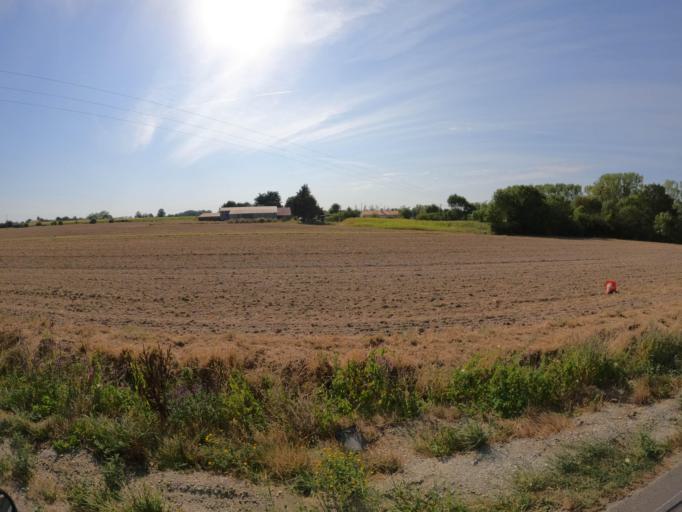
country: FR
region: Pays de la Loire
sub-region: Departement de la Vendee
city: Saint-Christophe-du-Ligneron
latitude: 46.8134
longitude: -1.7720
